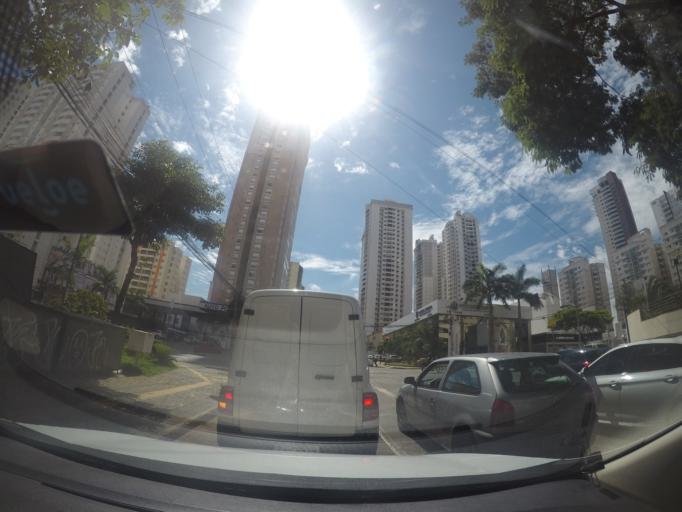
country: BR
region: Goias
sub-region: Goiania
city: Goiania
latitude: -16.7192
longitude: -49.2671
